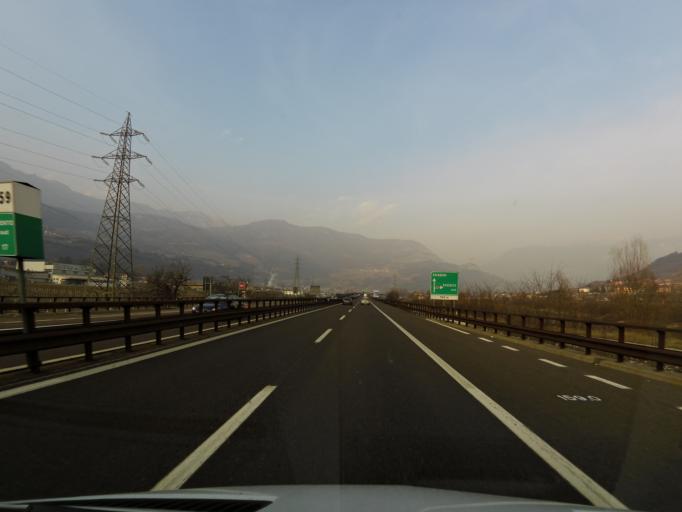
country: IT
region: Trentino-Alto Adige
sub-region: Provincia di Trento
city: Nogaredo
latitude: 45.9078
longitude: 11.0312
